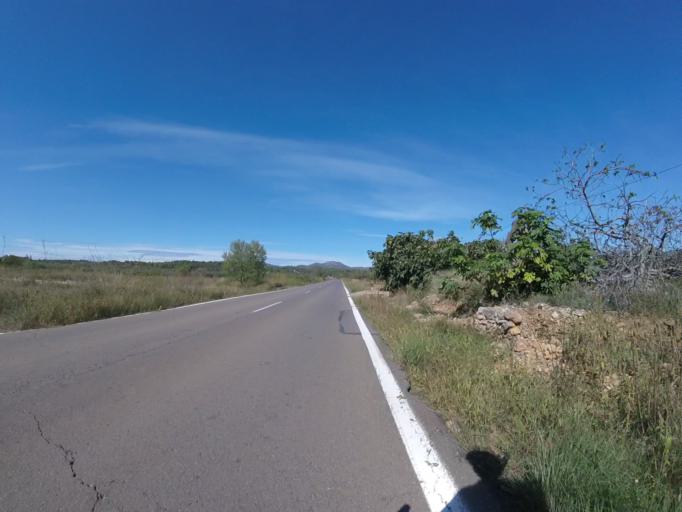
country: ES
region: Valencia
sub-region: Provincia de Castello
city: Benlloch
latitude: 40.2164
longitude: 0.0188
